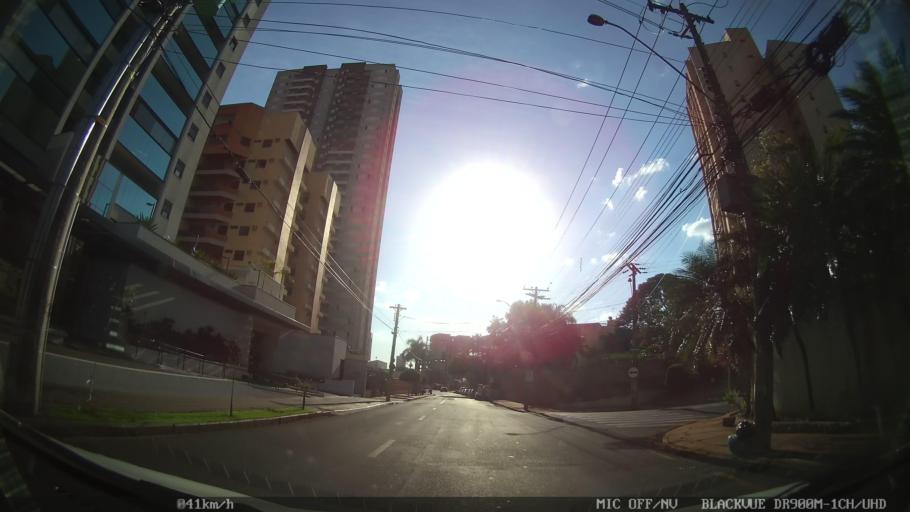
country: BR
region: Sao Paulo
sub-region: Ribeirao Preto
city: Ribeirao Preto
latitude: -21.1922
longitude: -47.7855
